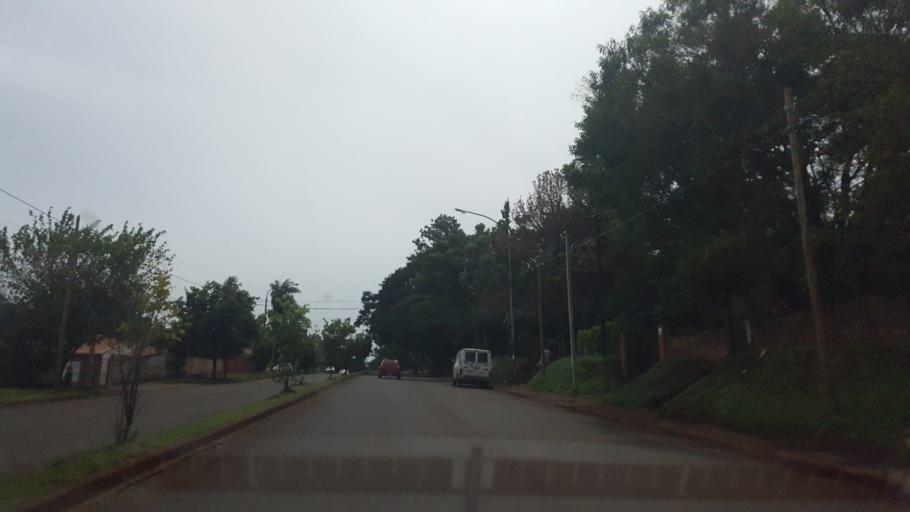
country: AR
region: Misiones
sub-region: Departamento de Capital
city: Posadas
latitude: -27.3980
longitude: -55.9437
